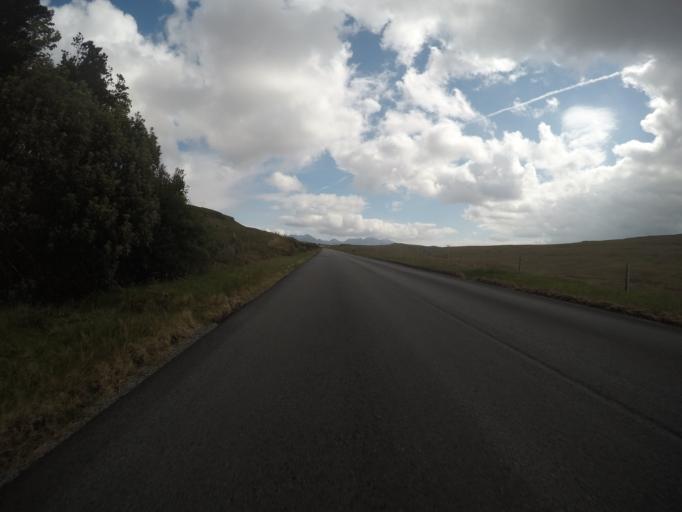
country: GB
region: Scotland
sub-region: Highland
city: Isle of Skye
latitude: 57.3239
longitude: -6.3310
